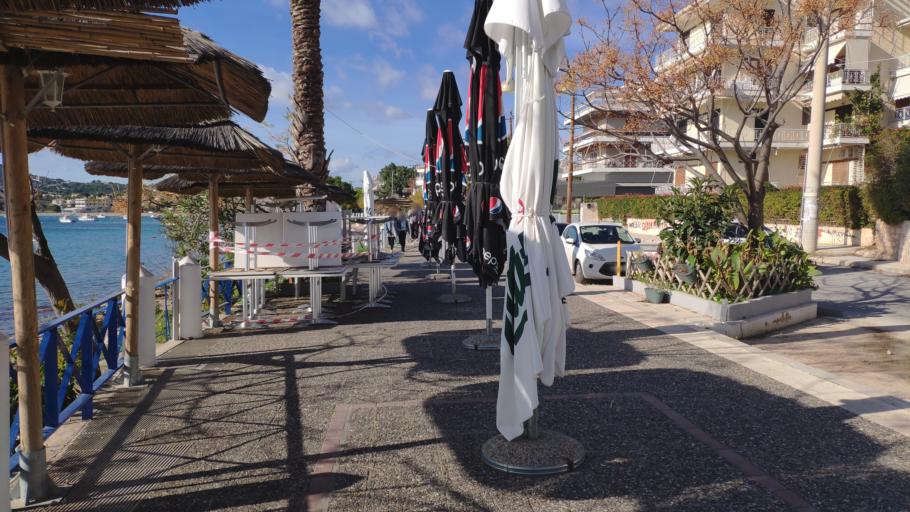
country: GR
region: Attica
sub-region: Nomarchia Anatolikis Attikis
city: Limin Mesoyaias
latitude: 37.8935
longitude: 24.0159
